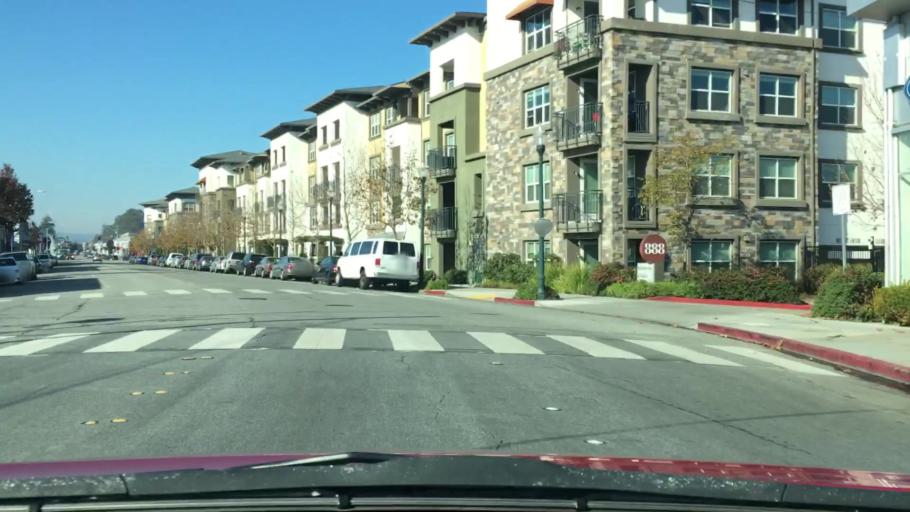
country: US
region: California
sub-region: San Mateo County
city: San Mateo
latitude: 37.5759
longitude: -122.3366
